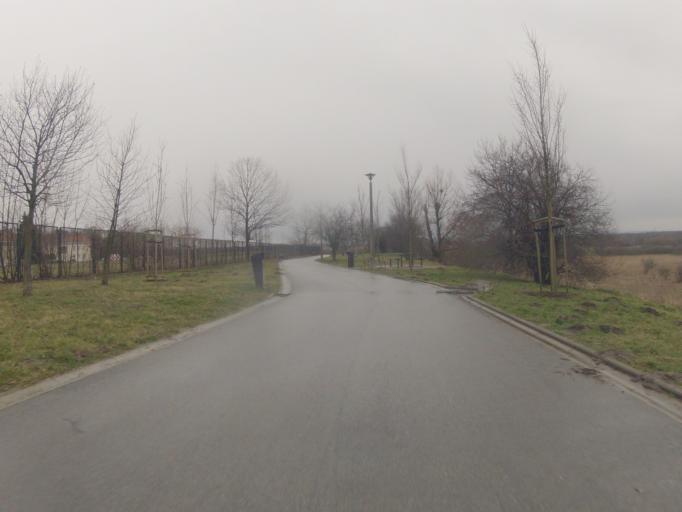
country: PL
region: Lesser Poland Voivodeship
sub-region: Powiat wielicki
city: Kokotow
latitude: 50.0658
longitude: 20.0427
